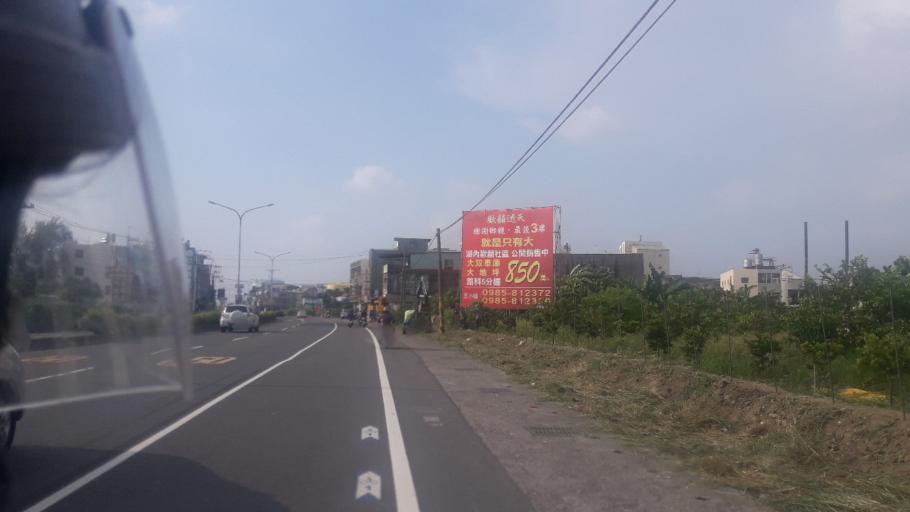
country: TW
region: Taiwan
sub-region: Tainan
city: Tainan
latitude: 22.8766
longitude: 120.2529
